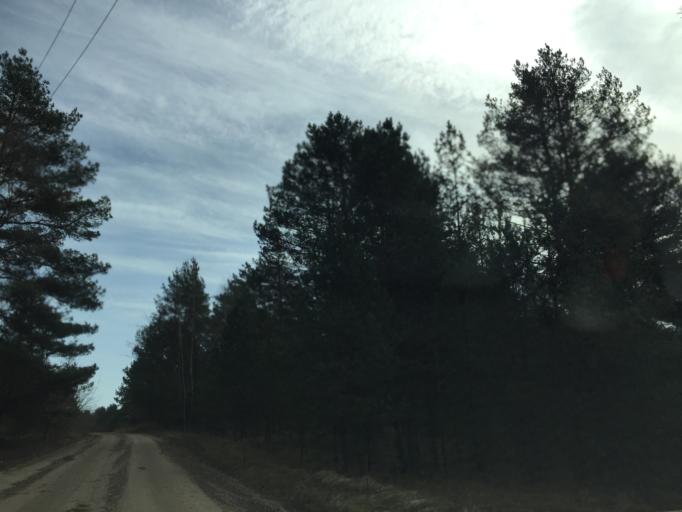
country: LV
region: Daugavpils
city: Daugavpils
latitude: 55.9036
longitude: 26.4757
